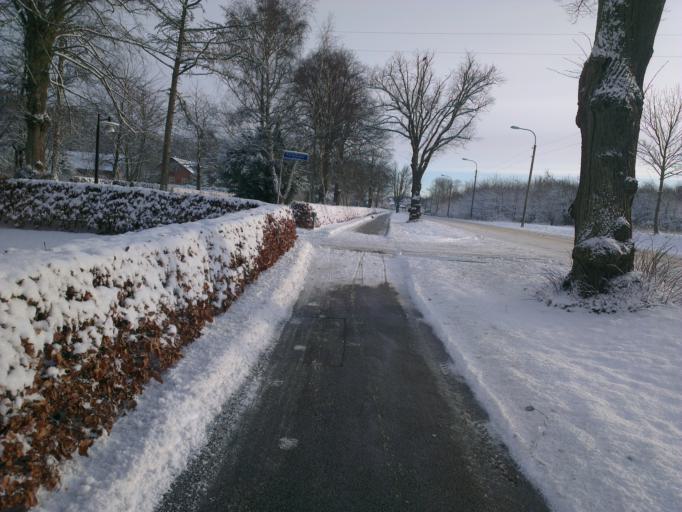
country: DK
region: Capital Region
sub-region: Frederikssund Kommune
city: Jaegerspris
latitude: 55.8550
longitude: 11.9756
